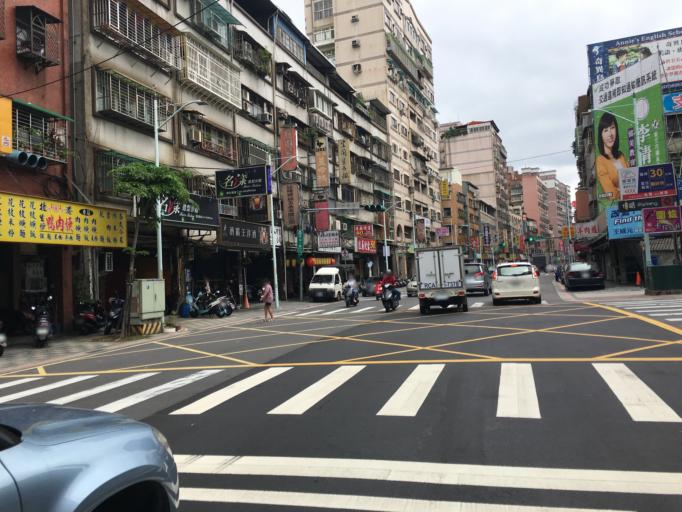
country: TW
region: Taipei
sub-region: Taipei
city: Banqiao
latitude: 25.0795
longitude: 121.4719
